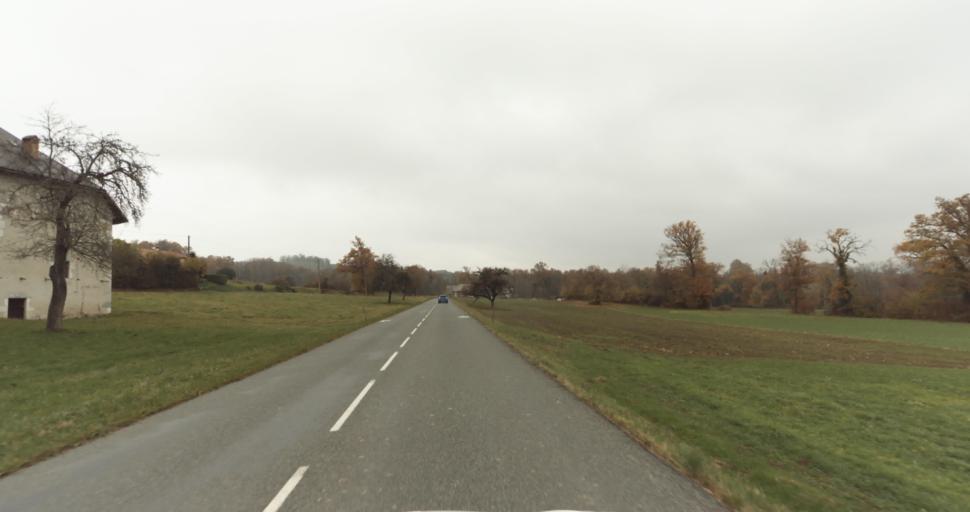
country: FR
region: Rhone-Alpes
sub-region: Departement de la Haute-Savoie
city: Cusy
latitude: 45.7874
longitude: 6.0125
